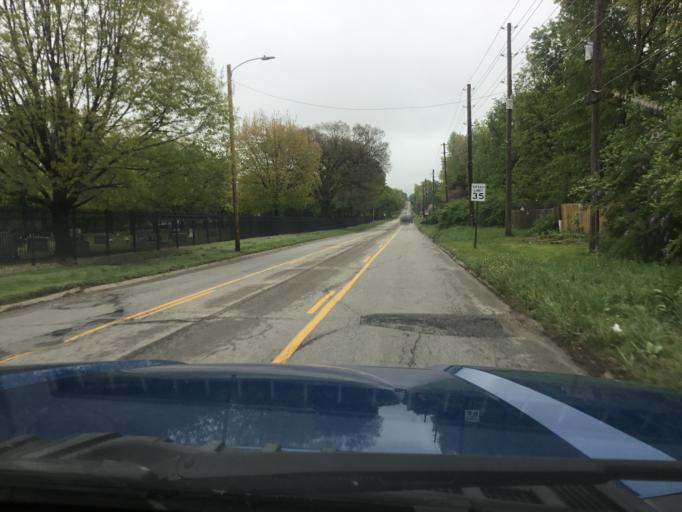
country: US
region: Kansas
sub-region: Shawnee County
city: Topeka
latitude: 39.0366
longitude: -95.7378
